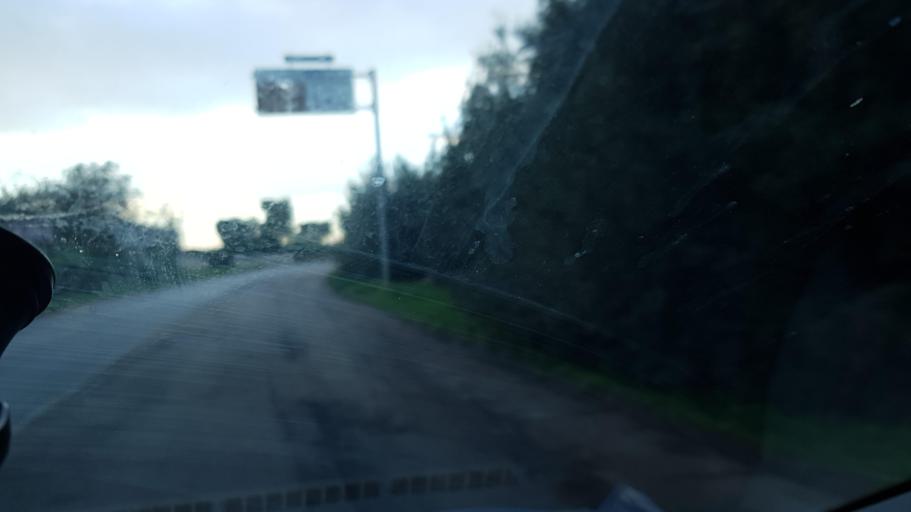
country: IT
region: Apulia
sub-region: Provincia di Brindisi
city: Ceglie Messapica
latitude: 40.6433
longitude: 17.5382
